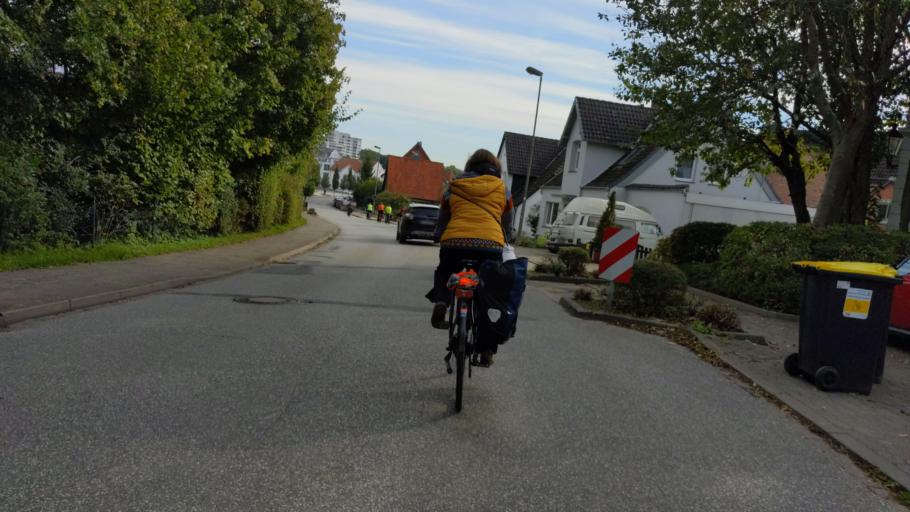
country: DE
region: Schleswig-Holstein
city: Reinfeld
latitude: 53.8320
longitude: 10.4805
